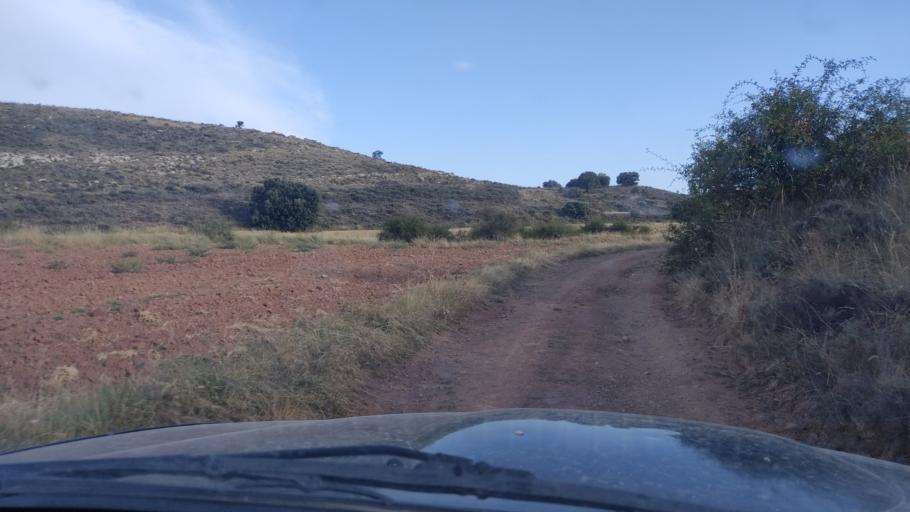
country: ES
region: Aragon
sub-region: Provincia de Teruel
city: Monforte de Moyuela
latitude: 41.0271
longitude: -1.0077
